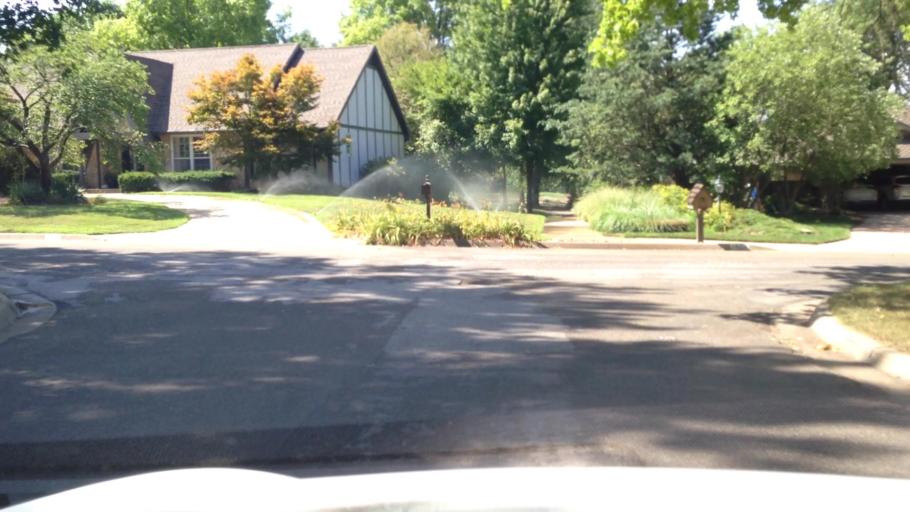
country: US
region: Kansas
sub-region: Douglas County
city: Lawrence
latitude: 38.9499
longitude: -95.2822
